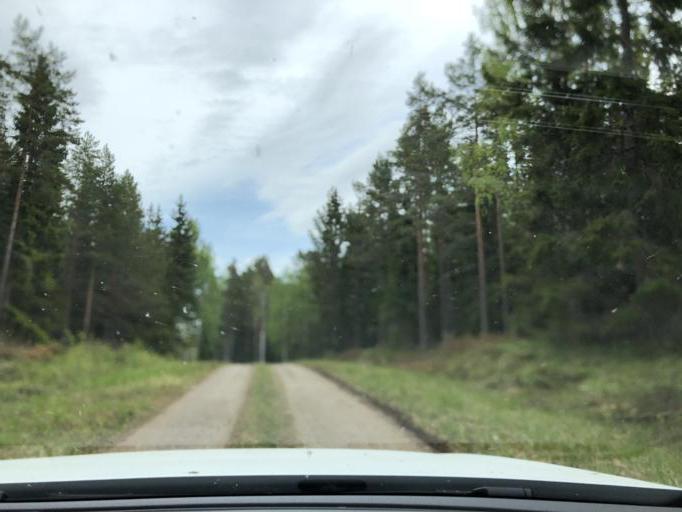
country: SE
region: Uppsala
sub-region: Heby Kommun
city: OEstervala
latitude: 60.3739
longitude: 17.2360
